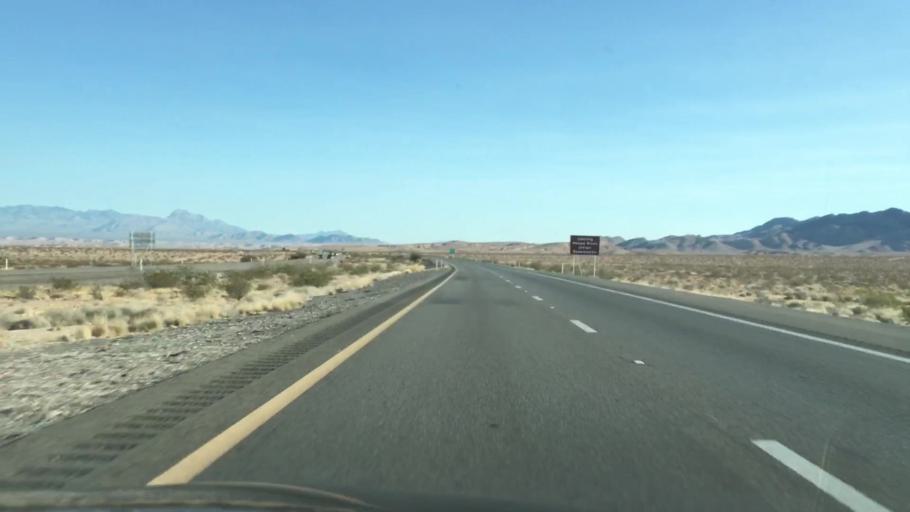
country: US
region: Nevada
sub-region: Clark County
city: Moapa Town
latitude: 36.5788
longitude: -114.6577
